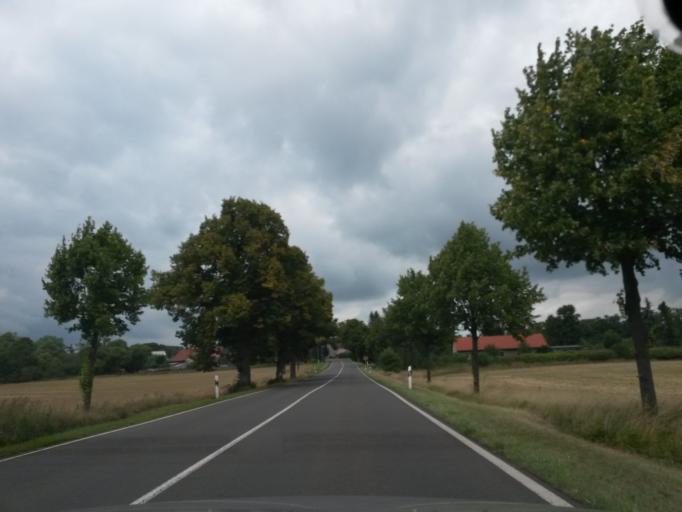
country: DE
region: Brandenburg
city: Angermunde
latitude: 53.1072
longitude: 13.9127
